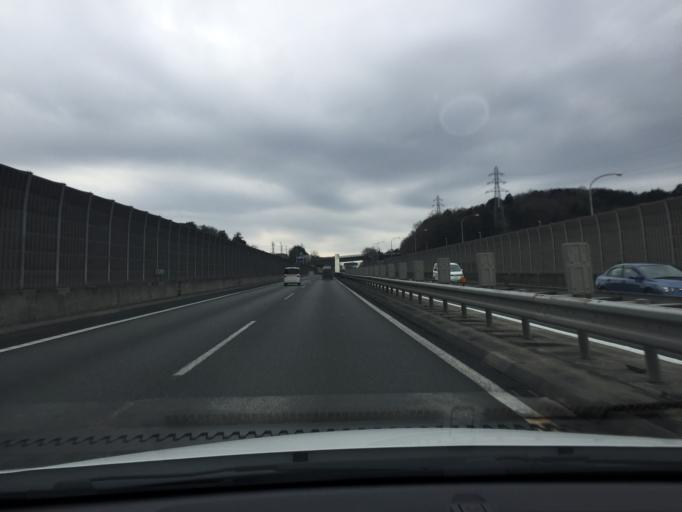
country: JP
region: Saitama
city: Sayama
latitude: 35.8398
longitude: 139.3701
